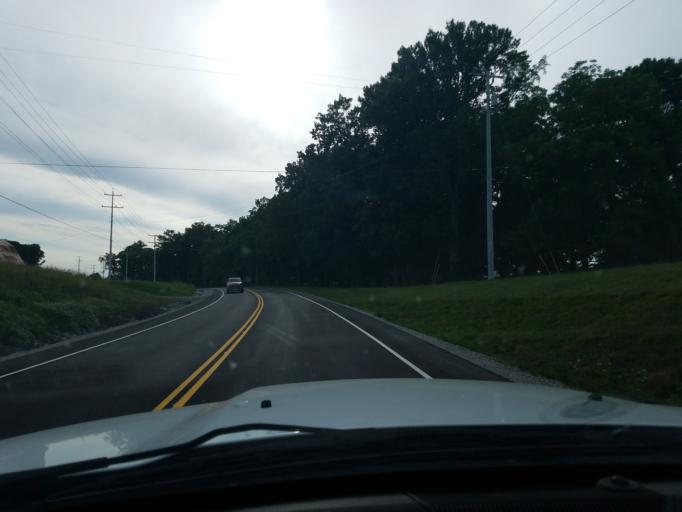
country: US
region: Tennessee
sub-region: Putnam County
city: Baxter
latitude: 36.1370
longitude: -85.5840
